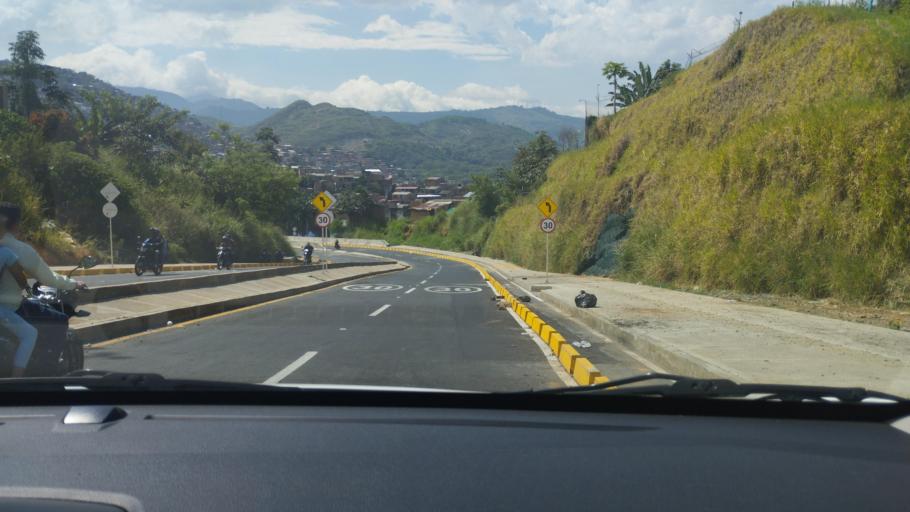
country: CO
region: Valle del Cauca
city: Cali
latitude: 3.3847
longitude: -76.5550
